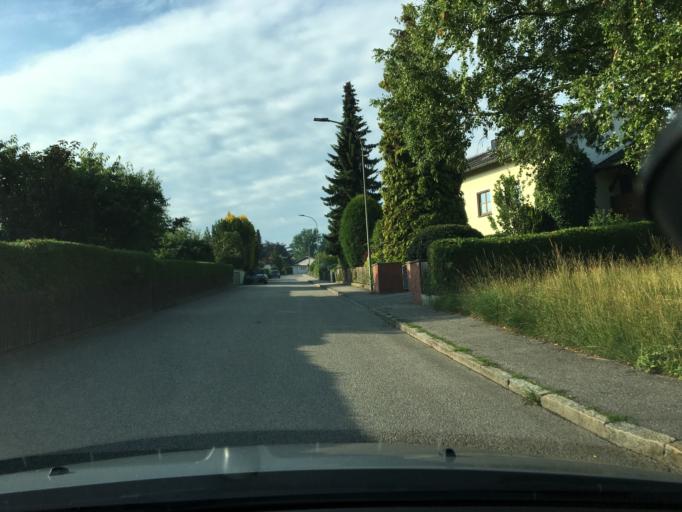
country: DE
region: Bavaria
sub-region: Lower Bavaria
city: Vilsbiburg
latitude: 48.4476
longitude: 12.3639
